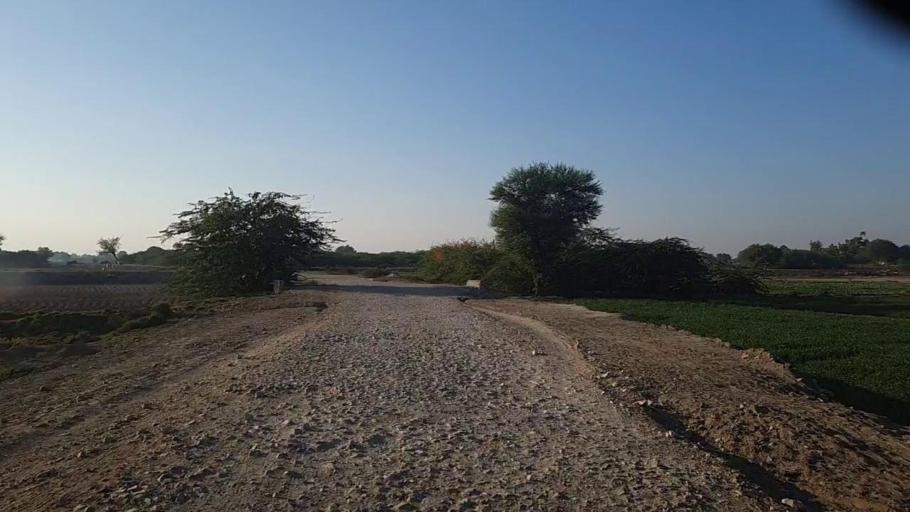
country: PK
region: Sindh
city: Pad Idan
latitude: 26.7344
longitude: 68.3445
